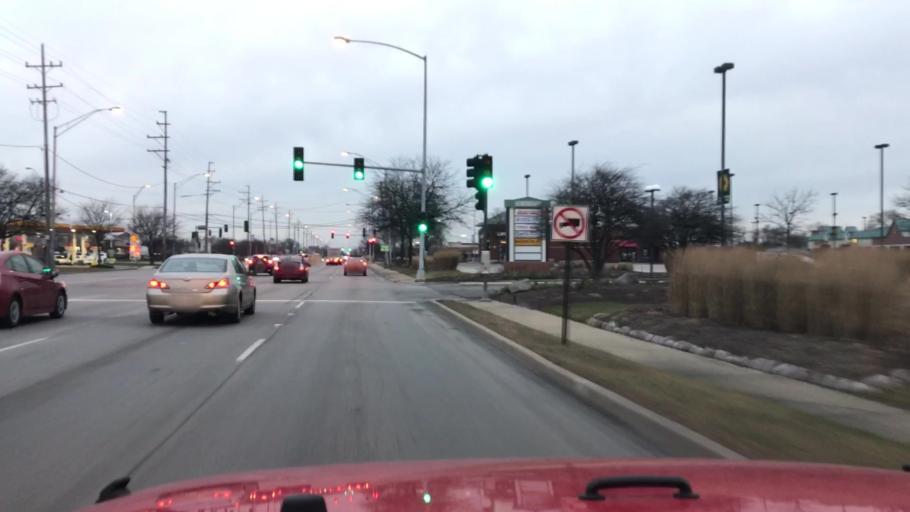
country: US
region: Illinois
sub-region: Cook County
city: Arlington Heights
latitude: 42.1117
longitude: -87.9788
